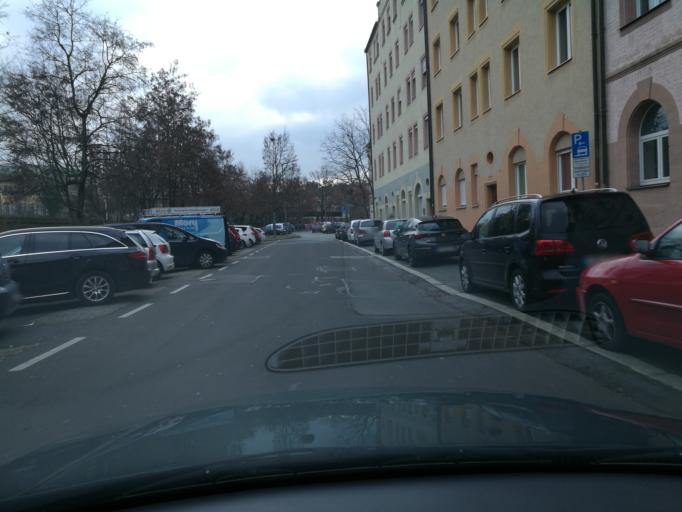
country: DE
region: Bavaria
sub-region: Regierungsbezirk Mittelfranken
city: Wetzendorf
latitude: 49.4639
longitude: 11.0568
